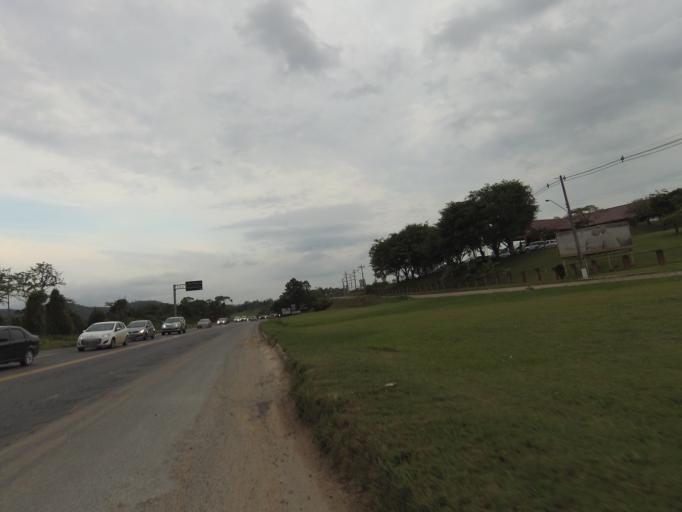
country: BR
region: Santa Catarina
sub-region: Blumenau
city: Blumenau
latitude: -26.8597
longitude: -49.0620
